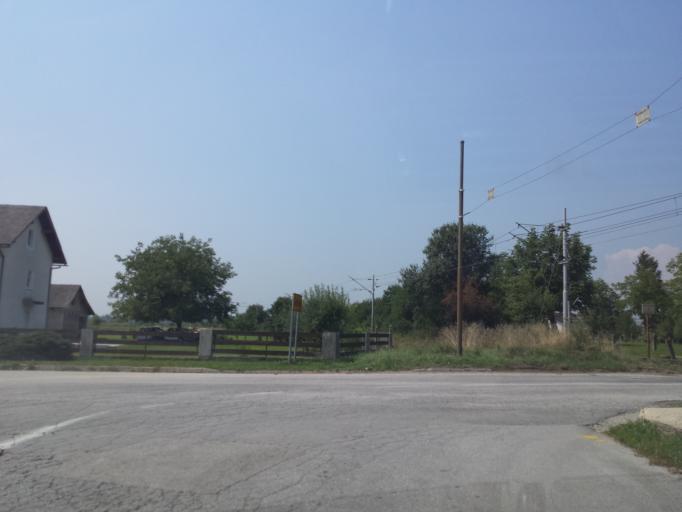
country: HR
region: Zagrebacka
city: Jastrebarsko
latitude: 45.6560
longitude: 15.6438
